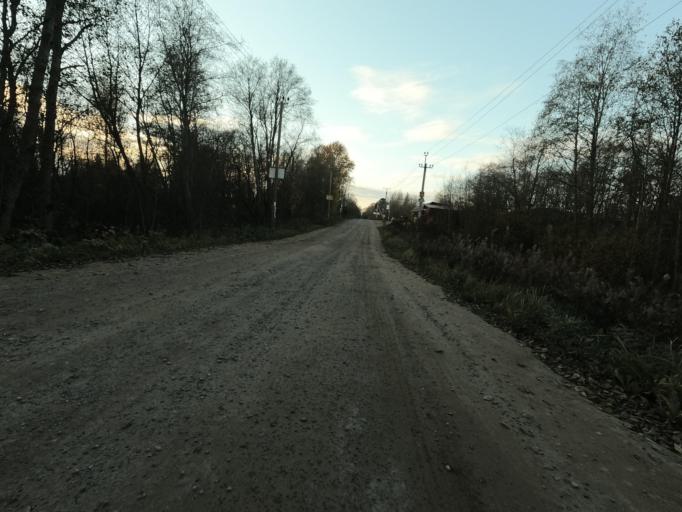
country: RU
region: Leningrad
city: Mga
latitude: 59.7644
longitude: 31.2484
